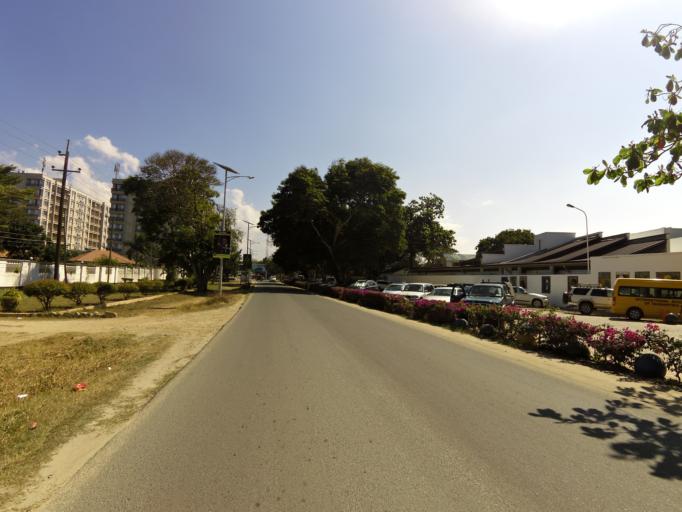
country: TZ
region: Dar es Salaam
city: Magomeni
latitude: -6.7603
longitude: 39.2786
